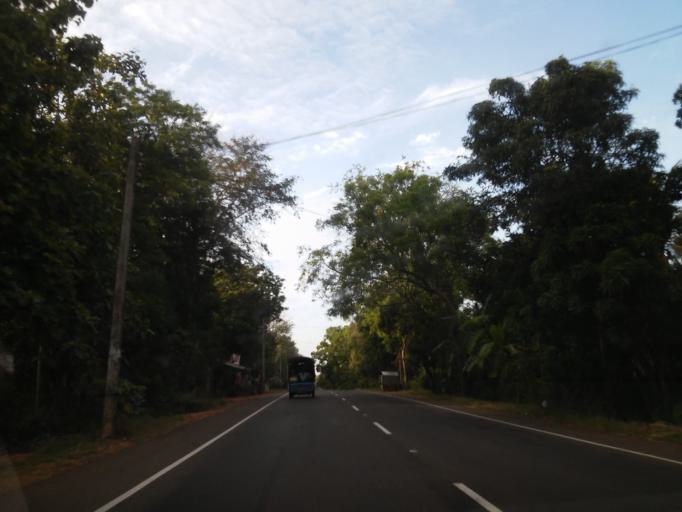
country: LK
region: North Central
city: Anuradhapura
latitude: 8.1672
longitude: 80.5358
